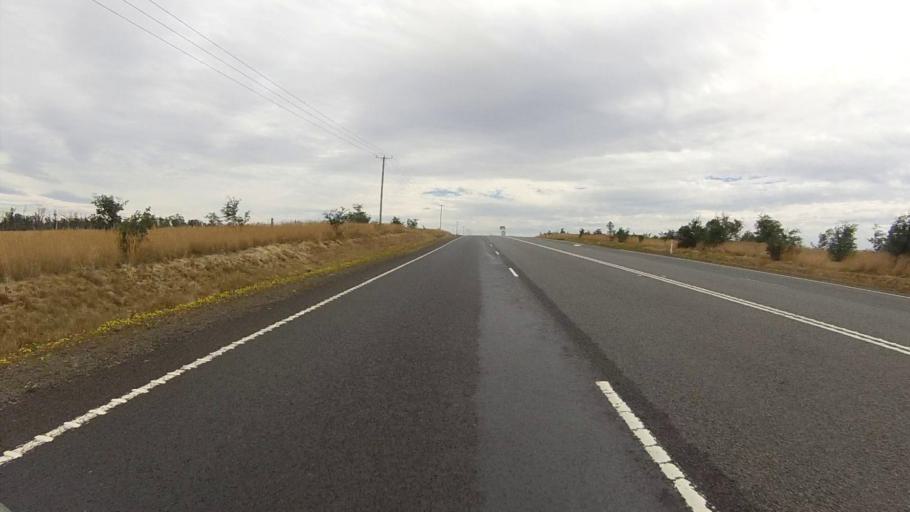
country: AU
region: Tasmania
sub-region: Northern Midlands
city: Evandale
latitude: -41.7167
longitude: 147.3077
